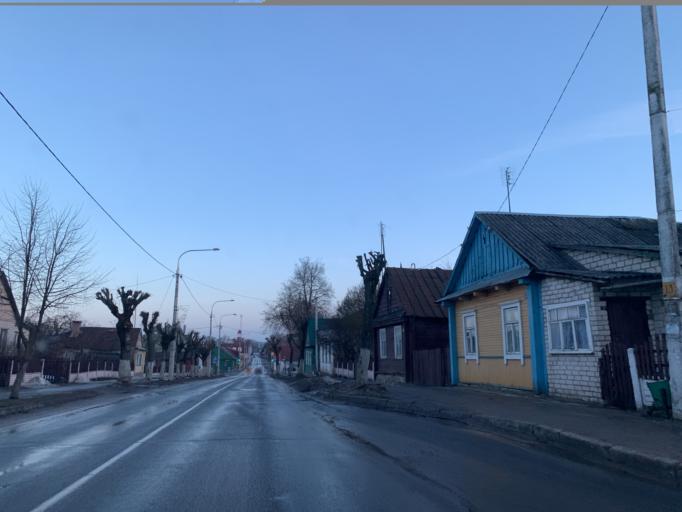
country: BY
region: Minsk
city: Nyasvizh
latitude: 53.2232
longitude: 26.6752
